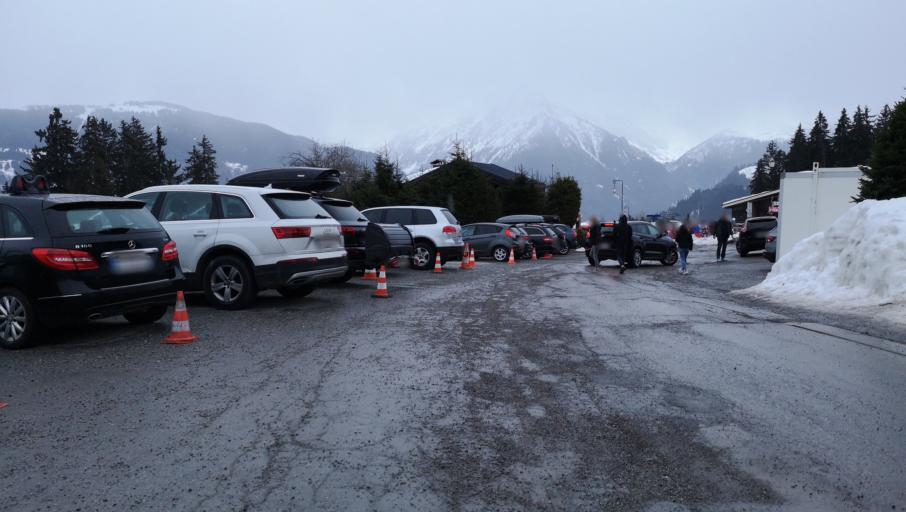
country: FR
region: Rhone-Alpes
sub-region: Departement de la Haute-Savoie
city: Saint-Gervais-les-Bains
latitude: 45.8746
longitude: 6.6876
